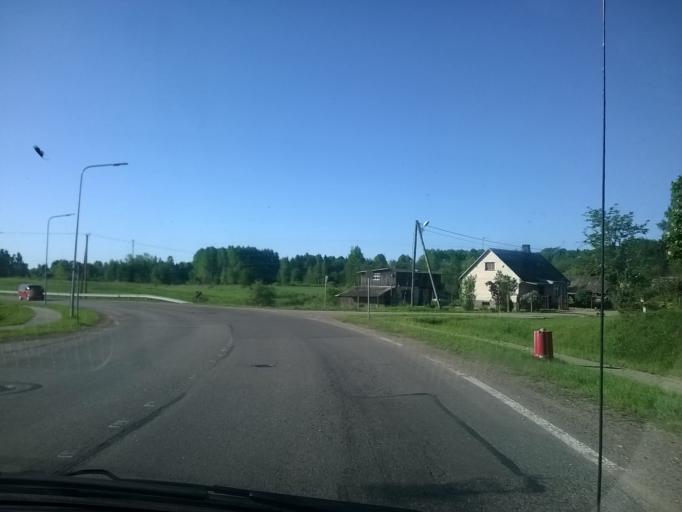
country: LV
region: Valkas Rajons
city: Valka
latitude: 57.7743
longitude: 25.9935
